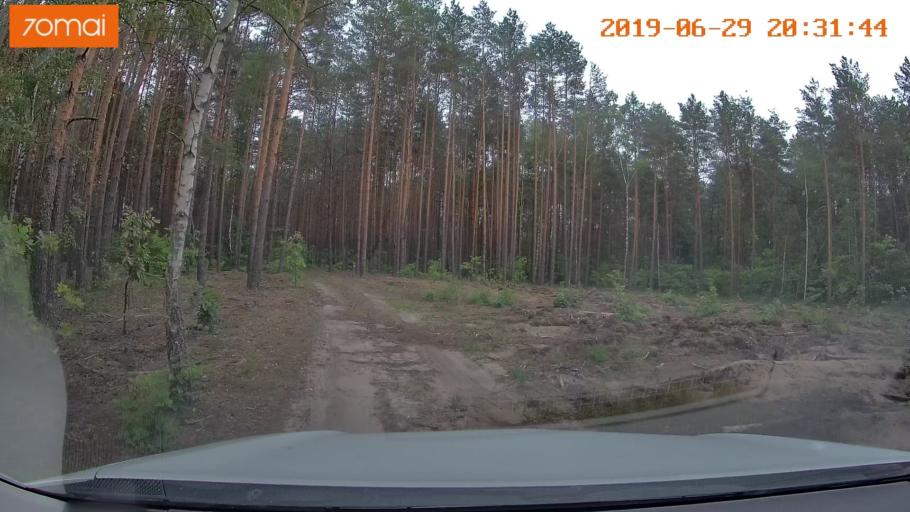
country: BY
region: Brest
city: Hantsavichy
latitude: 52.5141
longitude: 26.3452
